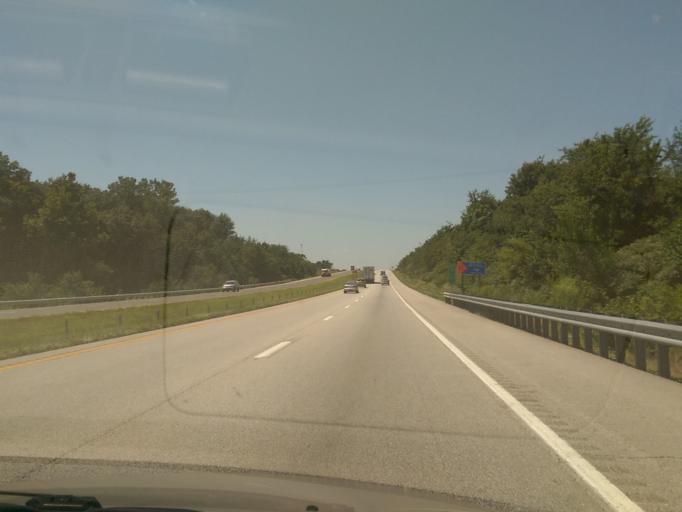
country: US
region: Missouri
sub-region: Saline County
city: Marshall
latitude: 38.9486
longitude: -93.0194
